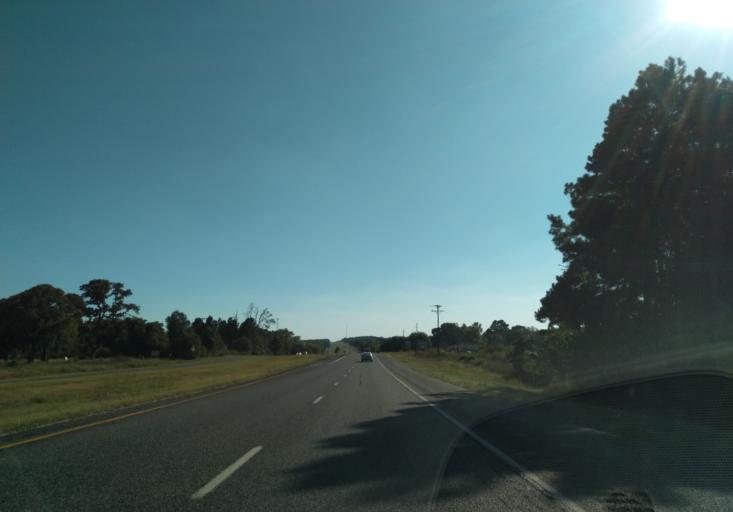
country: US
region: Texas
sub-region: Waller County
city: Hempstead
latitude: 30.1948
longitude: -96.0616
